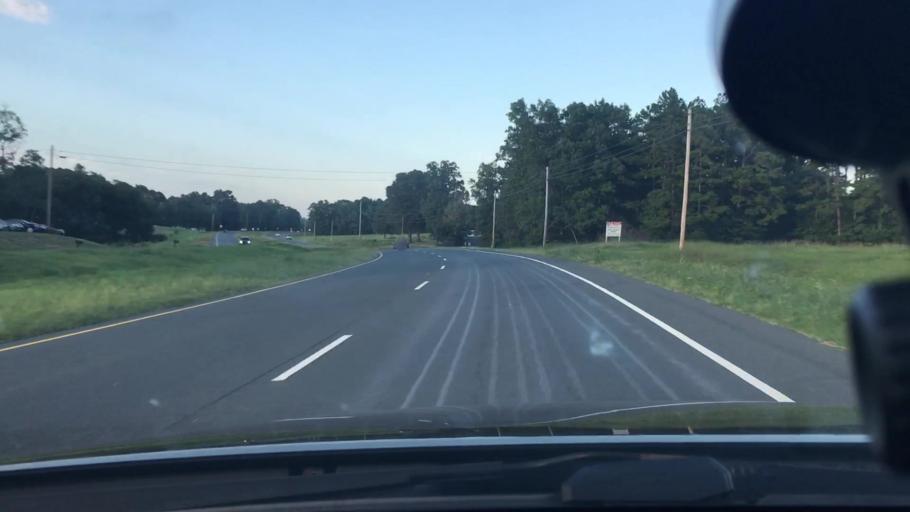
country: US
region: North Carolina
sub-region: Stanly County
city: Oakboro
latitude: 35.2882
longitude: -80.2921
